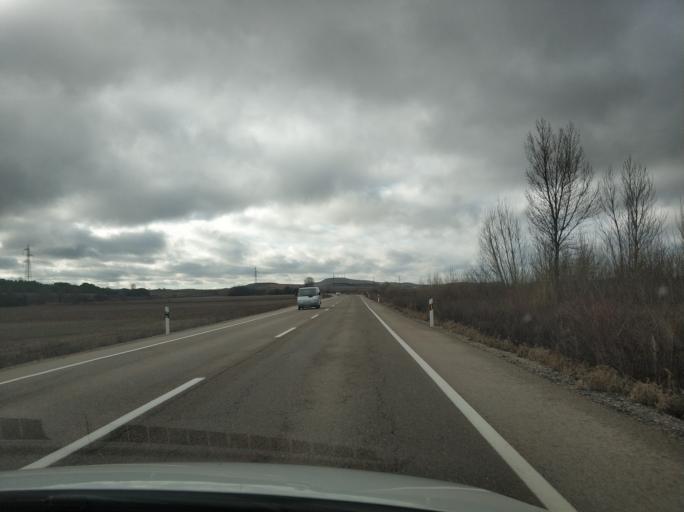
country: ES
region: Castille and Leon
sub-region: Provincia de Soria
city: San Esteban de Gormaz
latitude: 41.5669
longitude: -3.2359
